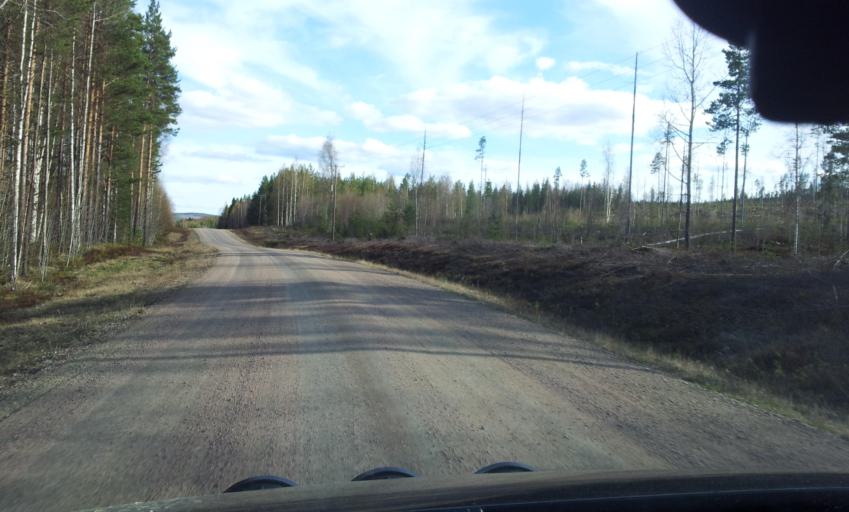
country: SE
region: Vaesternorrland
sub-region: Ange Kommun
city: Ange
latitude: 62.1633
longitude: 15.6590
